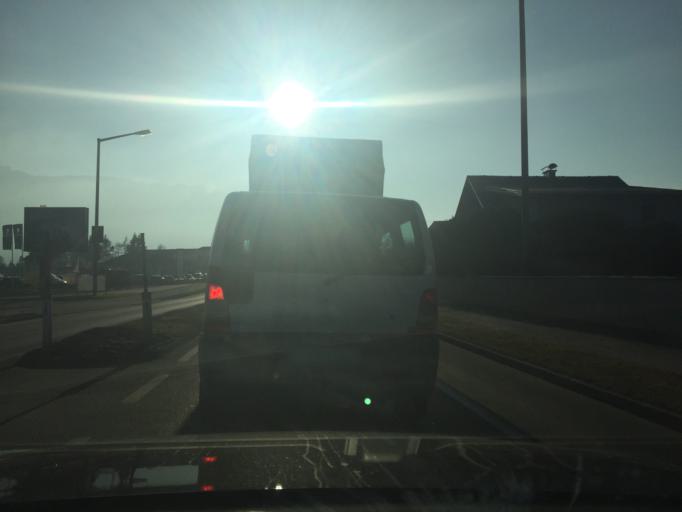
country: DE
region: Bavaria
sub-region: Upper Bavaria
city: Ainring
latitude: 47.7878
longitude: 12.9853
